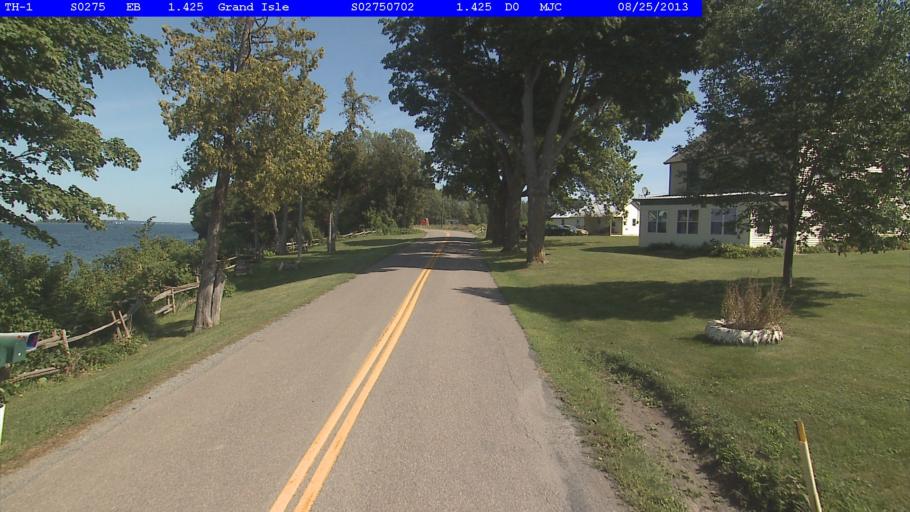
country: US
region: New York
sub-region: Clinton County
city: Cumberland Head
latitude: 44.7206
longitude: -73.3401
